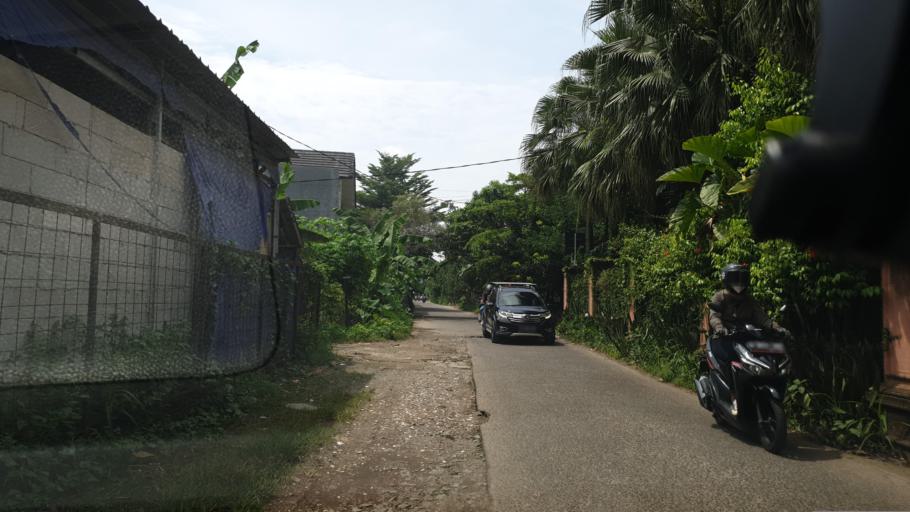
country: ID
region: West Java
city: Pamulang
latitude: -6.3644
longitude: 106.7641
